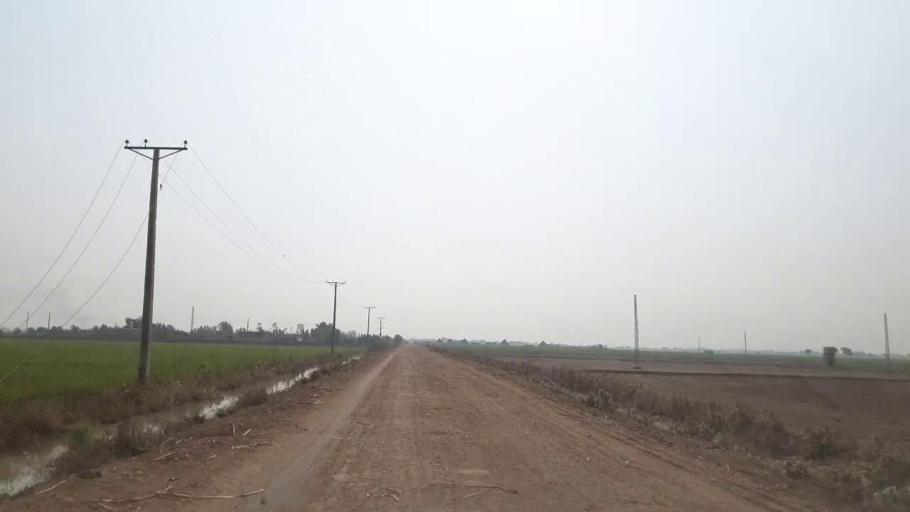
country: PK
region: Sindh
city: Mirpur Khas
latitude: 25.5457
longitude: 69.0597
